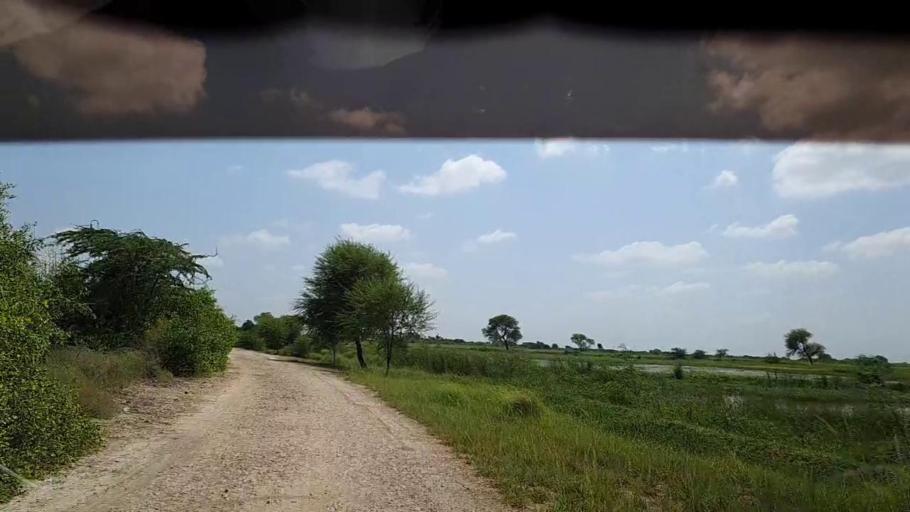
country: PK
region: Sindh
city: Kadhan
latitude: 24.5862
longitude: 68.9587
